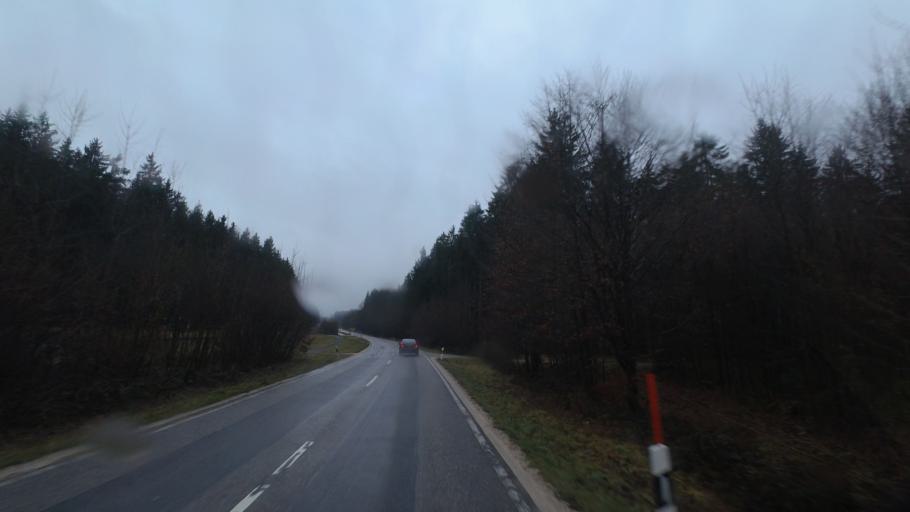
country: DE
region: Bavaria
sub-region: Upper Bavaria
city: Surberg
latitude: 47.8878
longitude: 12.6777
